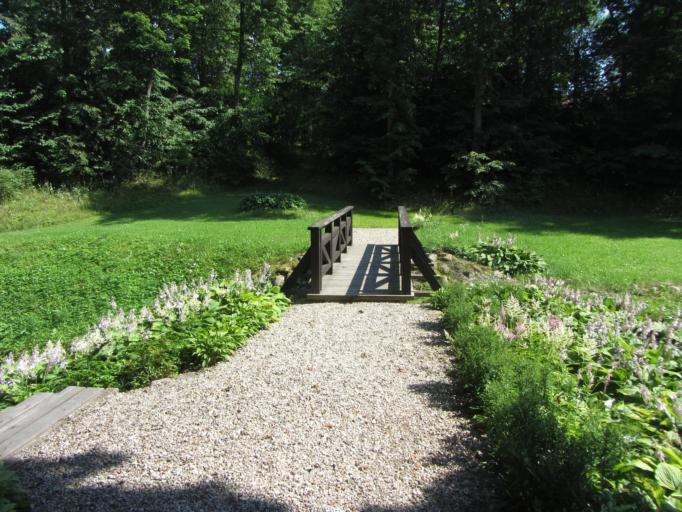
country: LT
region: Vilnius County
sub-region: Vilnius
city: Vilnius
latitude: 54.7307
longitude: 25.2916
